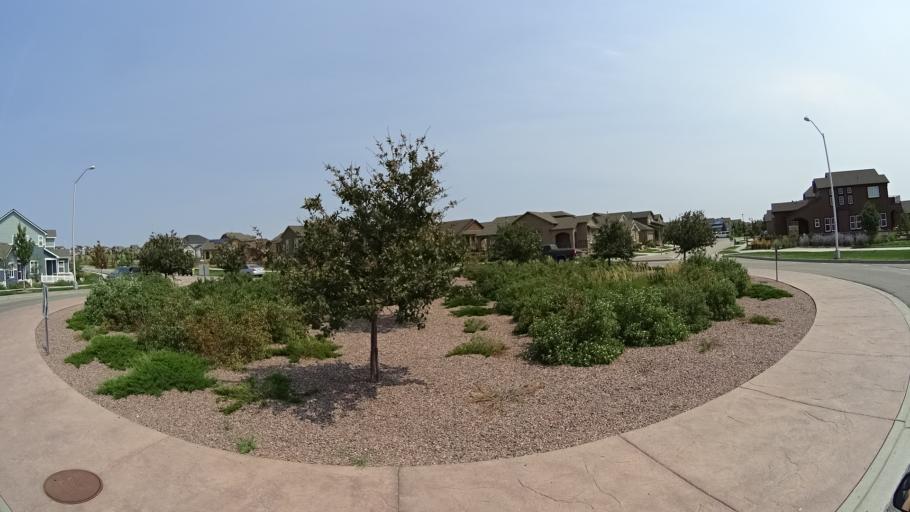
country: US
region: Colorado
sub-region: El Paso County
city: Black Forest
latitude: 38.9601
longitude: -104.7266
